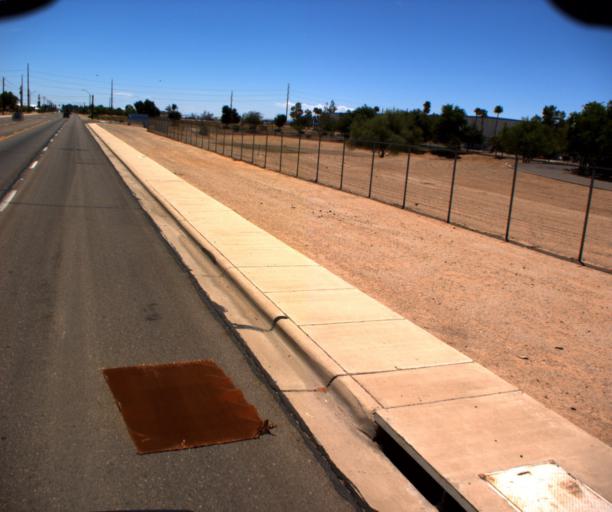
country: US
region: Arizona
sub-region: Pinal County
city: Casa Grande
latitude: 32.8794
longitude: -111.7804
